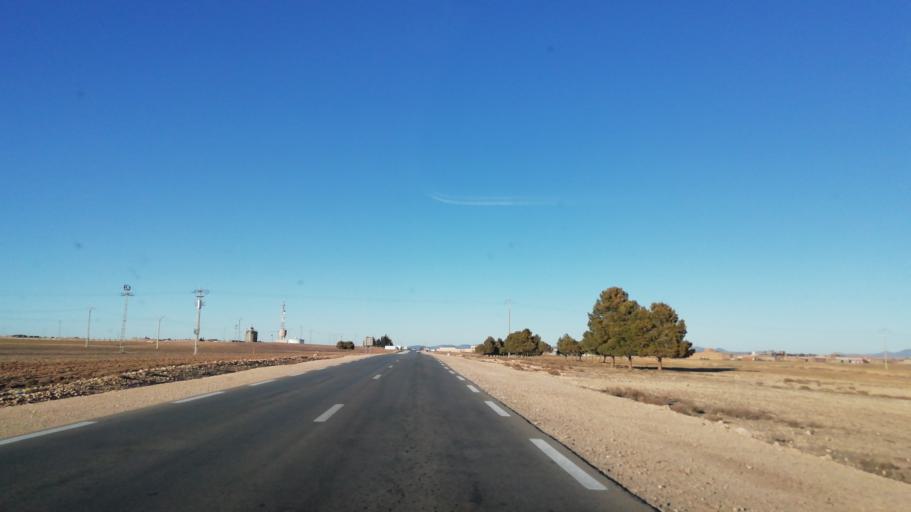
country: DZ
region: Tlemcen
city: Sebdou
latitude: 34.4738
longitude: -1.2717
